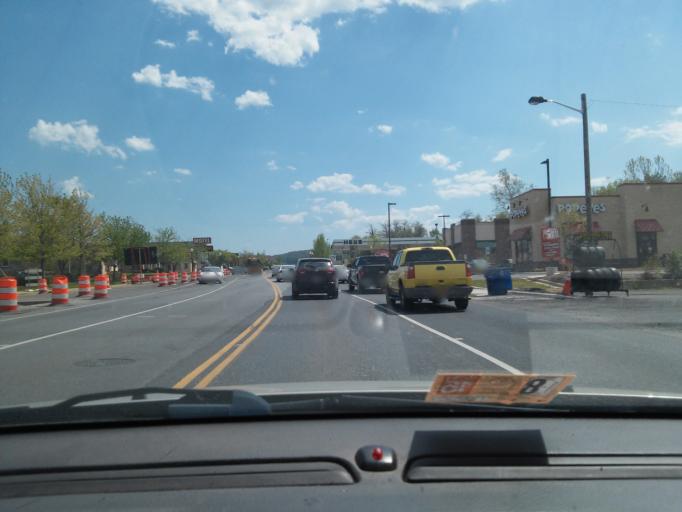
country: US
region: Virginia
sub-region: Warren County
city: Front Royal
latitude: 38.9387
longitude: -78.1994
